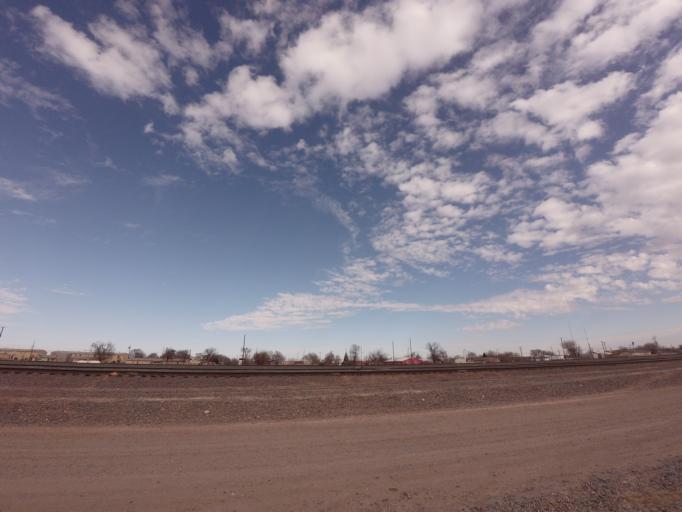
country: US
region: New Mexico
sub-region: Curry County
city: Clovis
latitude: 34.3983
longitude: -103.2292
